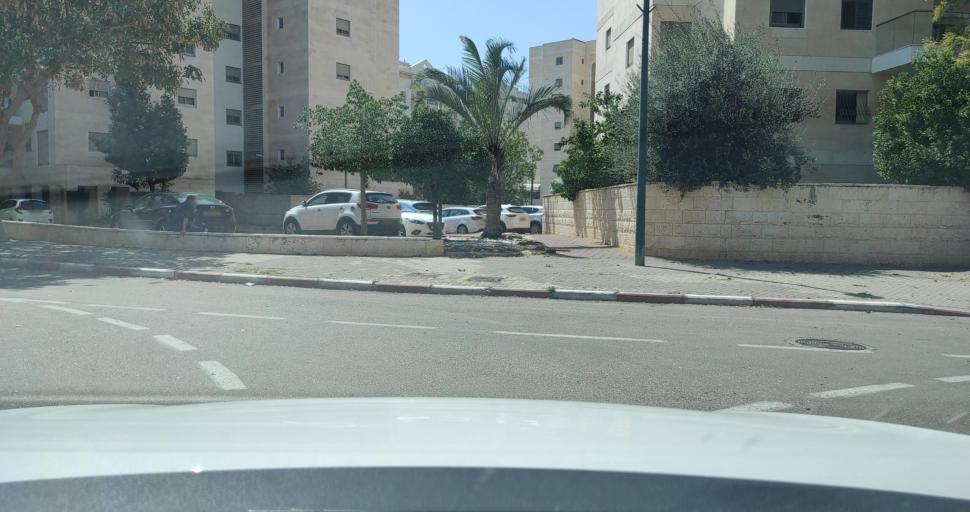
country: IL
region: Central District
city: Nordiyya
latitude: 32.2985
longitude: 34.8714
